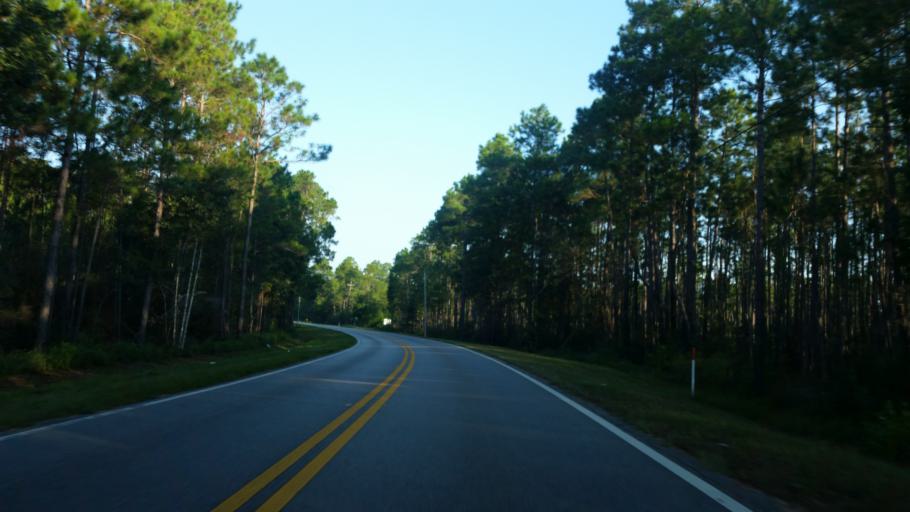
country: US
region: Florida
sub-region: Santa Rosa County
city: East Milton
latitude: 30.6037
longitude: -87.0081
